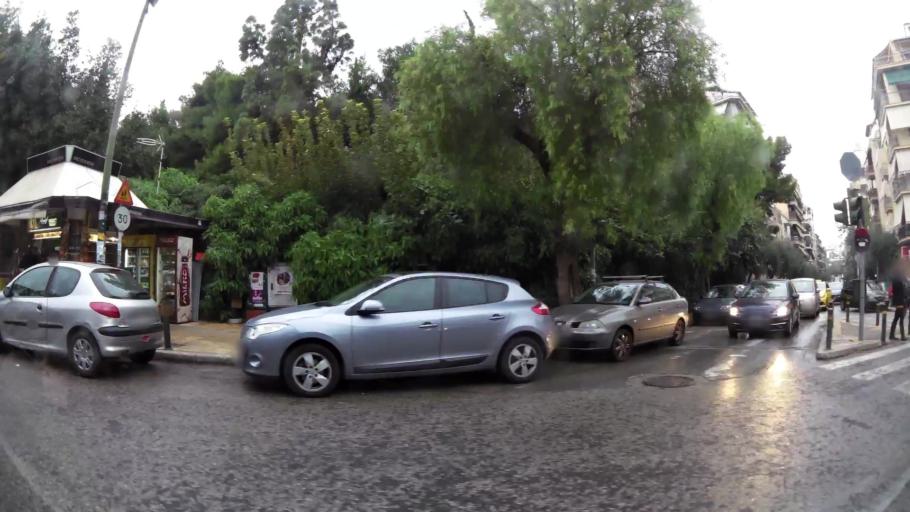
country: GR
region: Attica
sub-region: Nomarchia Athinas
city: Vyronas
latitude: 37.9703
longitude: 23.7473
